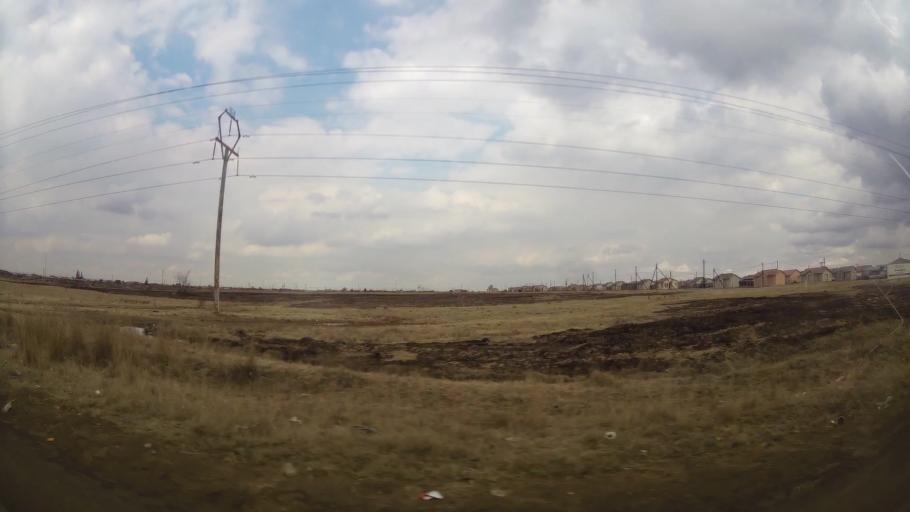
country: ZA
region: Orange Free State
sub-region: Fezile Dabi District Municipality
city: Sasolburg
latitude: -26.8561
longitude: 27.8661
